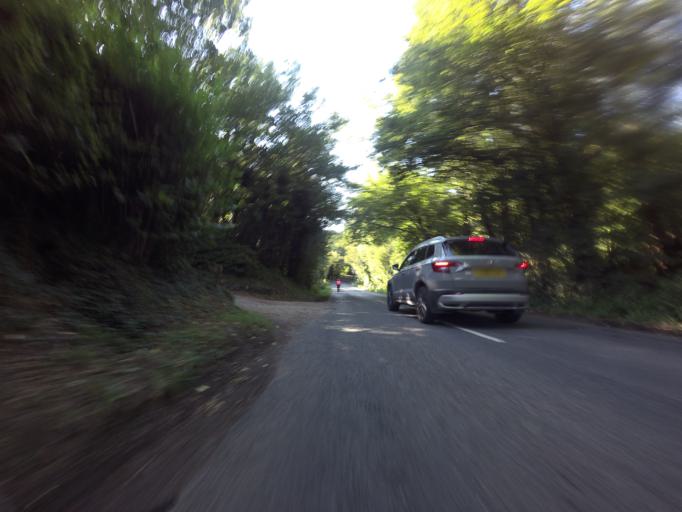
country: GB
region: England
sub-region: Kent
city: Tenterden
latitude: 51.0483
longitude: 0.6960
